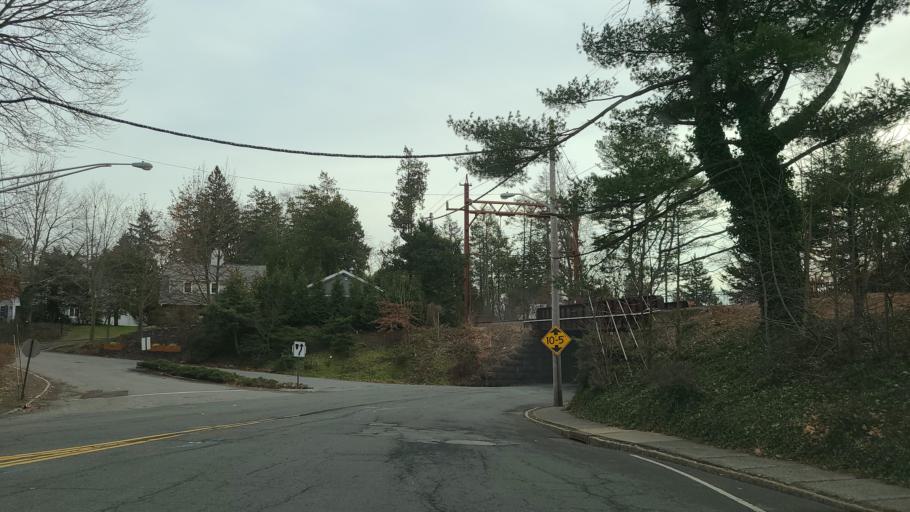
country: US
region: New Jersey
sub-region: Union County
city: Springfield
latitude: 40.7252
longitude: -74.3228
